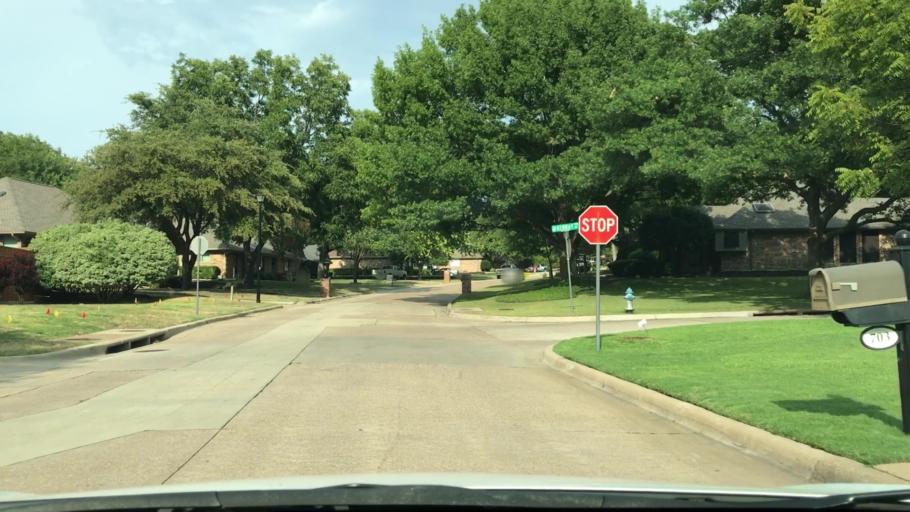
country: US
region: Texas
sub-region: Rockwall County
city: Rockwall
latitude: 32.9276
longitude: -96.4663
